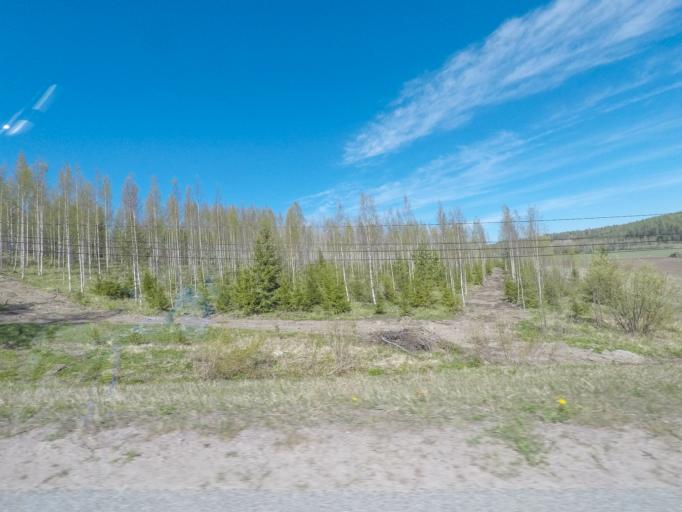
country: FI
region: Uusimaa
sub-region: Helsinki
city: Sammatti
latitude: 60.3911
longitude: 23.8068
